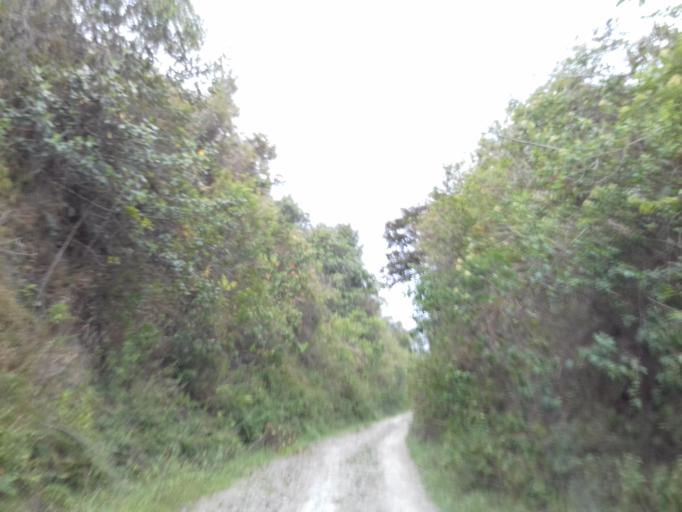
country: CO
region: Tolima
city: Cajamarca
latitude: 4.5281
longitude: -75.4134
